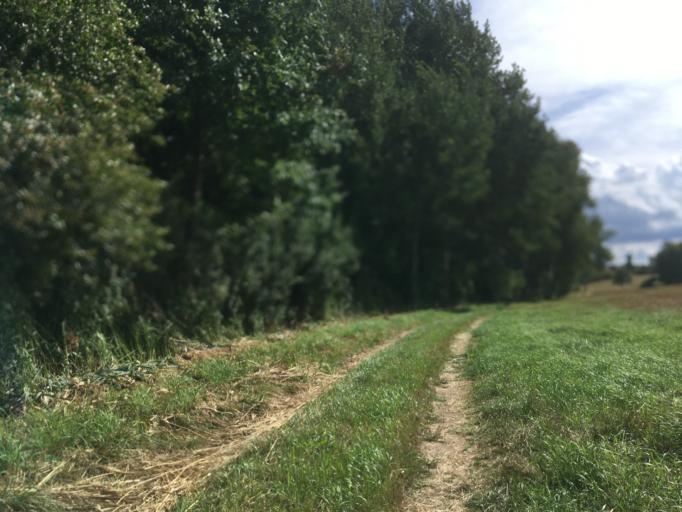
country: DE
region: Brandenburg
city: Gerswalde
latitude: 53.1299
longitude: 13.7867
